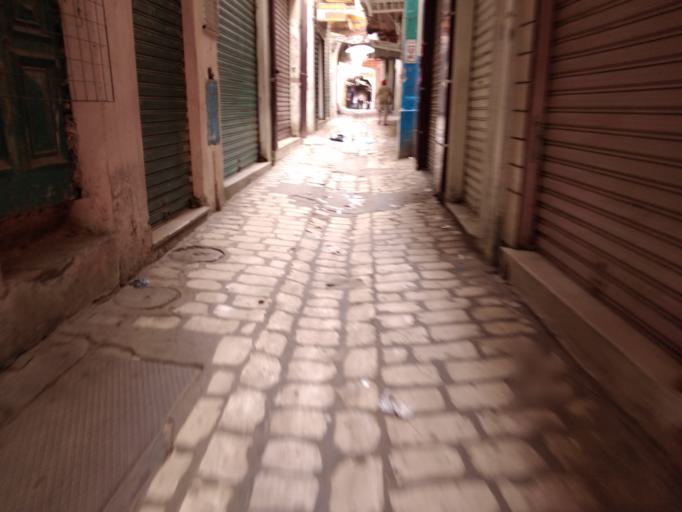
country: TN
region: Safaqis
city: Sfax
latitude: 34.7358
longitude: 10.7617
